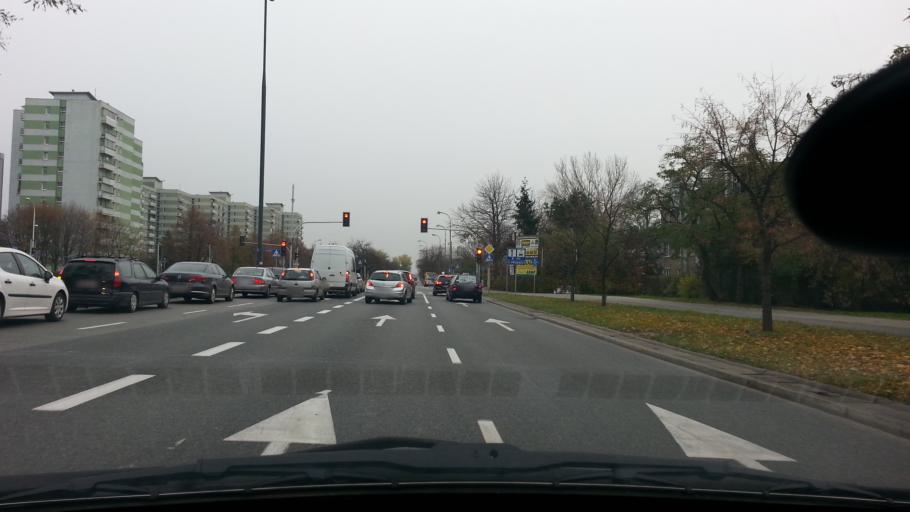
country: PL
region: Masovian Voivodeship
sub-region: Warszawa
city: Targowek
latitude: 52.2919
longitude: 21.0177
